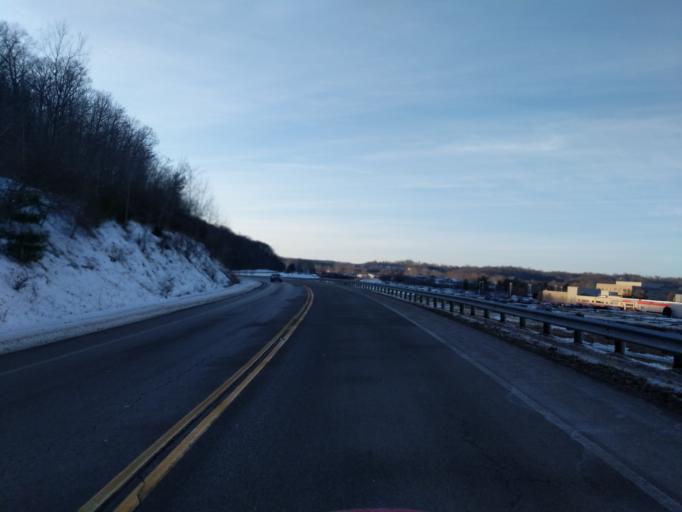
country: US
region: Ohio
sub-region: Athens County
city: Athens
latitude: 39.3245
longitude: -82.1132
